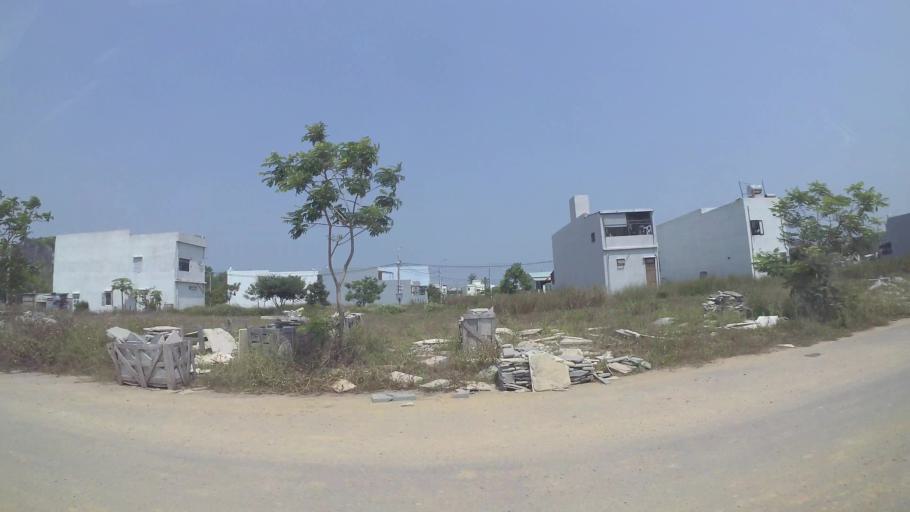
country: VN
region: Da Nang
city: Ngu Hanh Son
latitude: 15.9959
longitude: 108.2605
